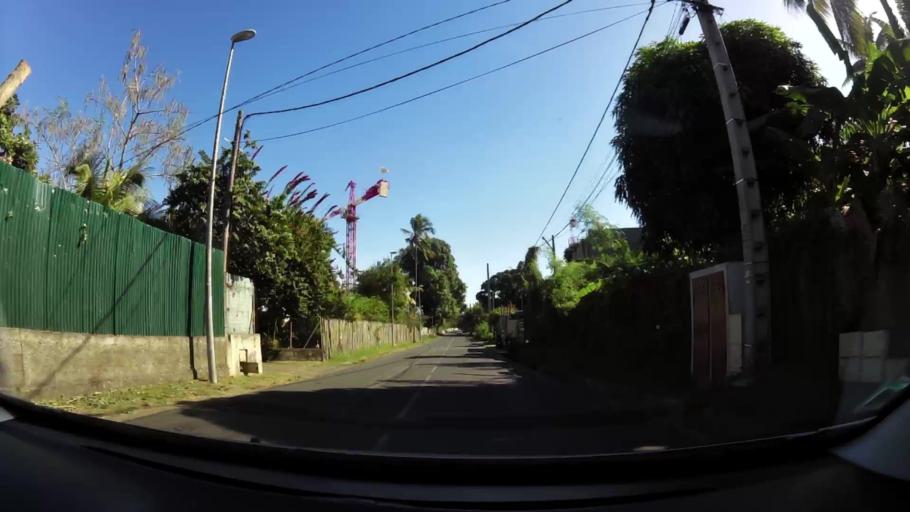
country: YT
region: Pamandzi
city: Pamandzi
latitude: -12.7948
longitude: 45.2777
